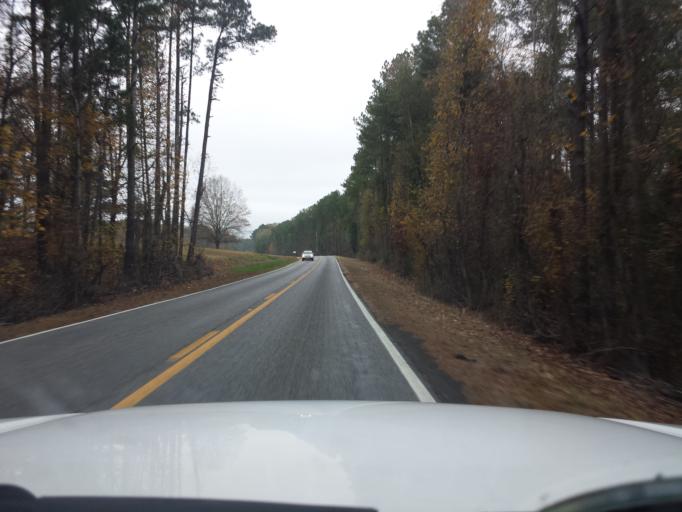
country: US
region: Mississippi
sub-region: Madison County
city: Canton
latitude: 32.4798
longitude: -89.9162
